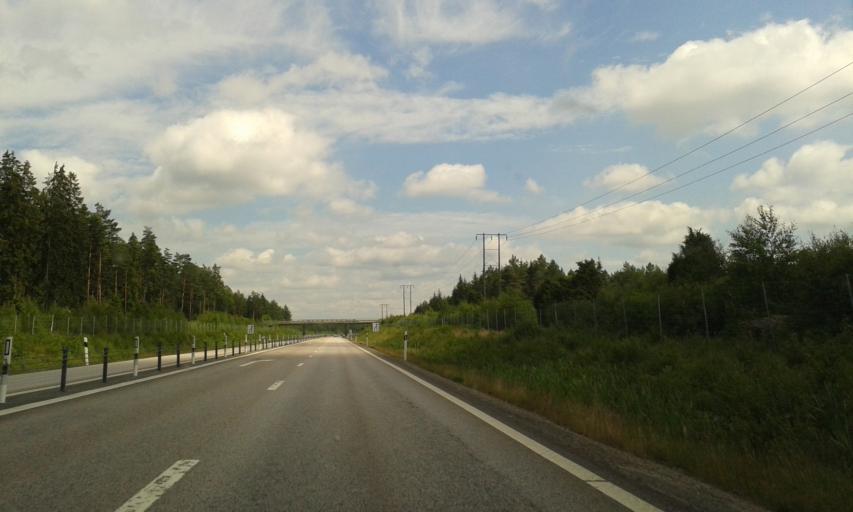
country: SE
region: Kronoberg
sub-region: Alvesta Kommun
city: Alvesta
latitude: 56.9185
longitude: 14.5221
